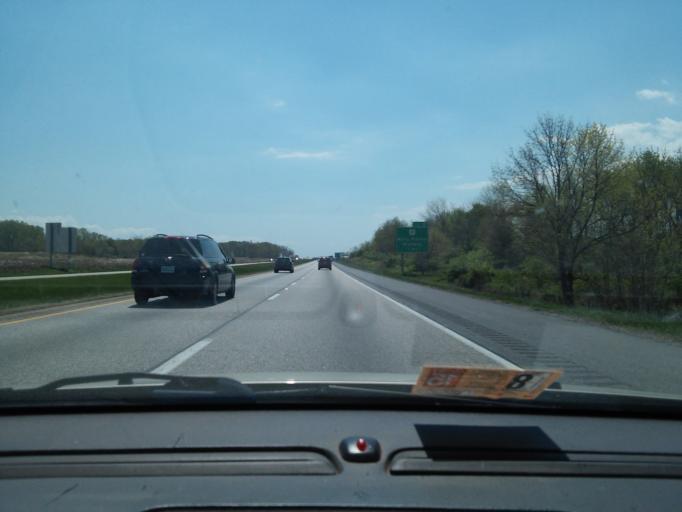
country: US
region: Pennsylvania
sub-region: Franklin County
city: Greencastle
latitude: 39.7730
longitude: -77.7191
